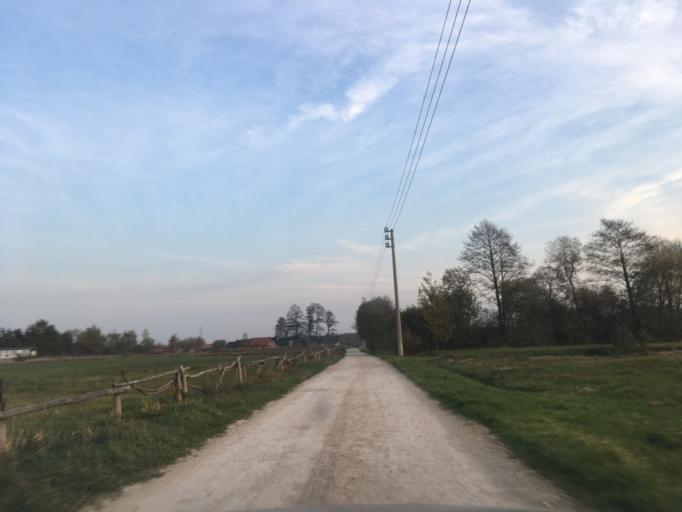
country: PL
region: Masovian Voivodeship
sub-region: Powiat piaseczynski
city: Lesznowola
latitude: 52.0508
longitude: 20.9254
